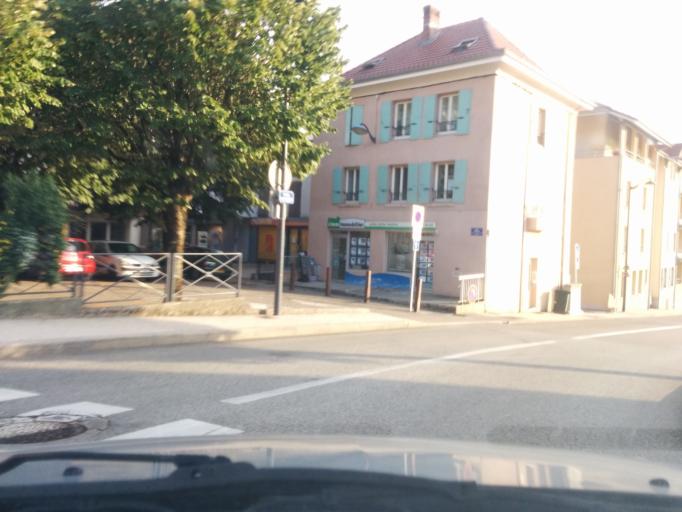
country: FR
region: Rhone-Alpes
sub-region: Departement de l'Isere
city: Voreppe
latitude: 45.2978
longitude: 5.6364
